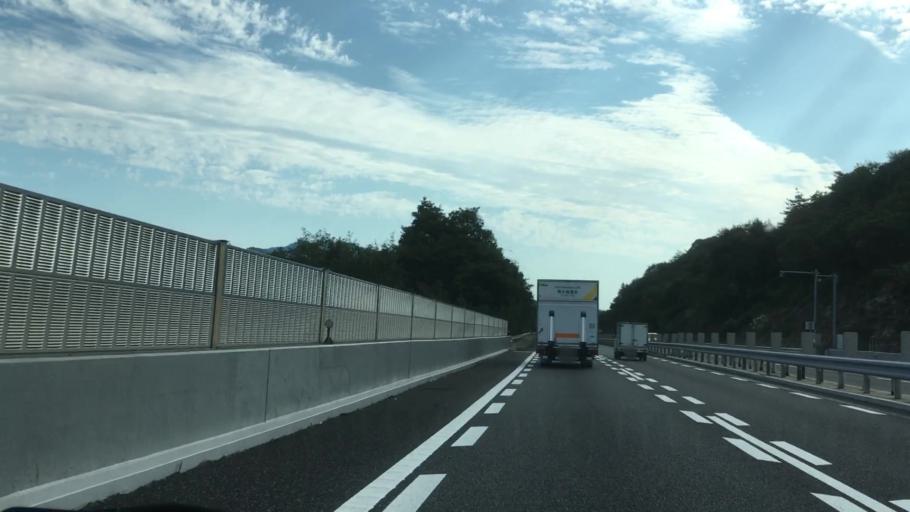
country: JP
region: Hiroshima
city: Ono-hara
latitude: 34.3124
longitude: 132.2805
